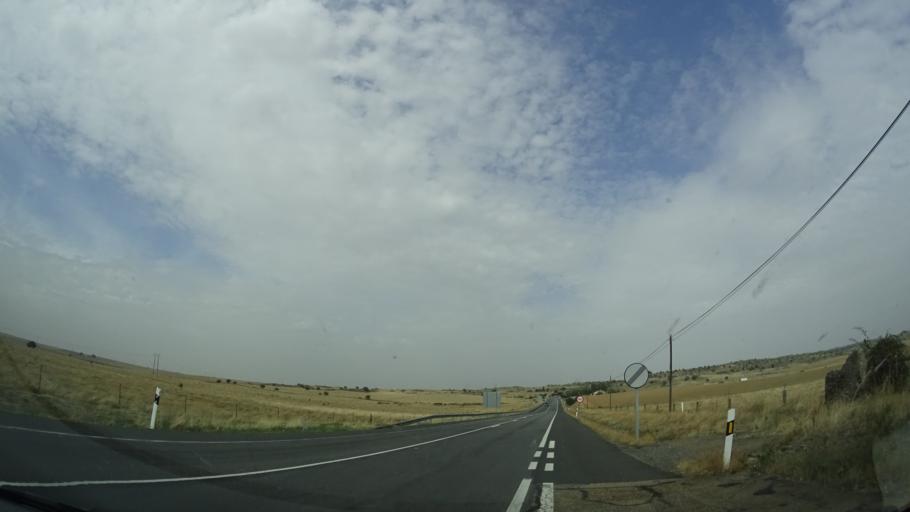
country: ES
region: Extremadura
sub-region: Provincia de Caceres
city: Trujillo
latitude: 39.4120
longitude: -5.8918
